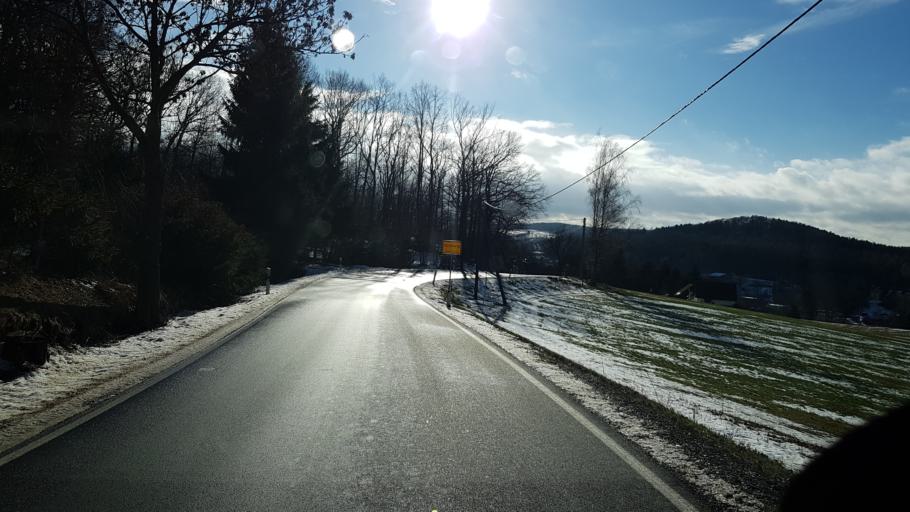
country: DE
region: Saxony
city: Kirchberg
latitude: 50.6339
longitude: 12.5278
